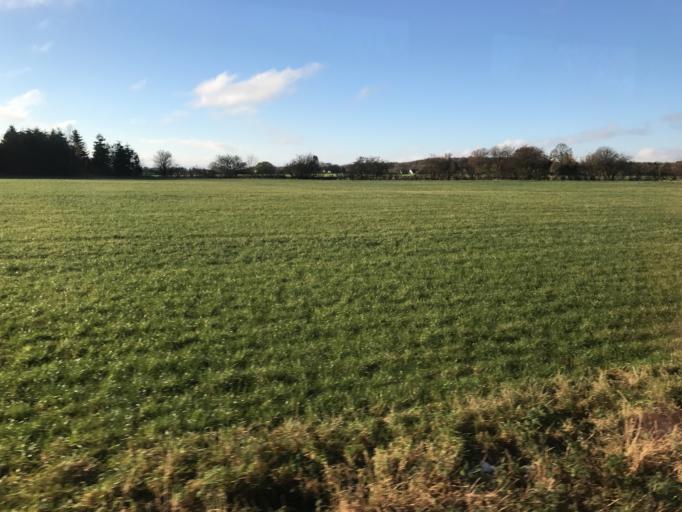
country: DK
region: Zealand
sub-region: Stevns Kommune
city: Store Heddinge
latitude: 55.3219
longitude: 12.3682
